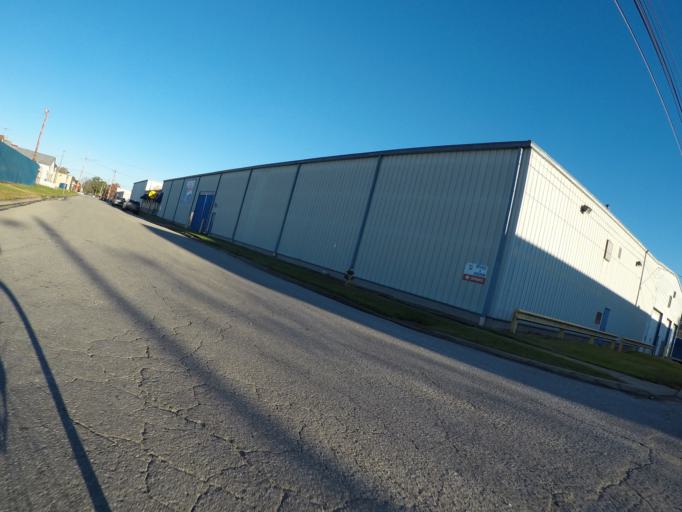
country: US
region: West Virginia
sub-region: Cabell County
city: Huntington
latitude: 38.4075
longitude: -82.4813
